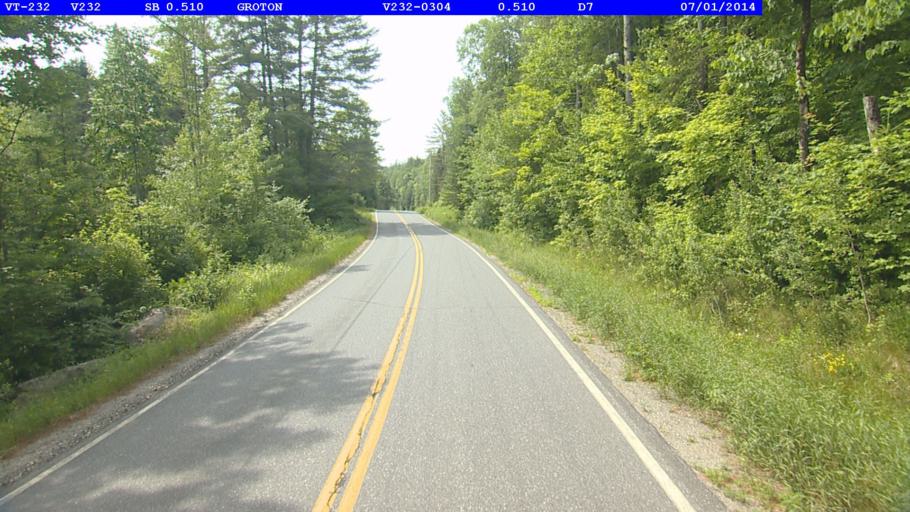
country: US
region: New Hampshire
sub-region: Grafton County
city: Woodsville
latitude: 44.2264
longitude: -72.2288
